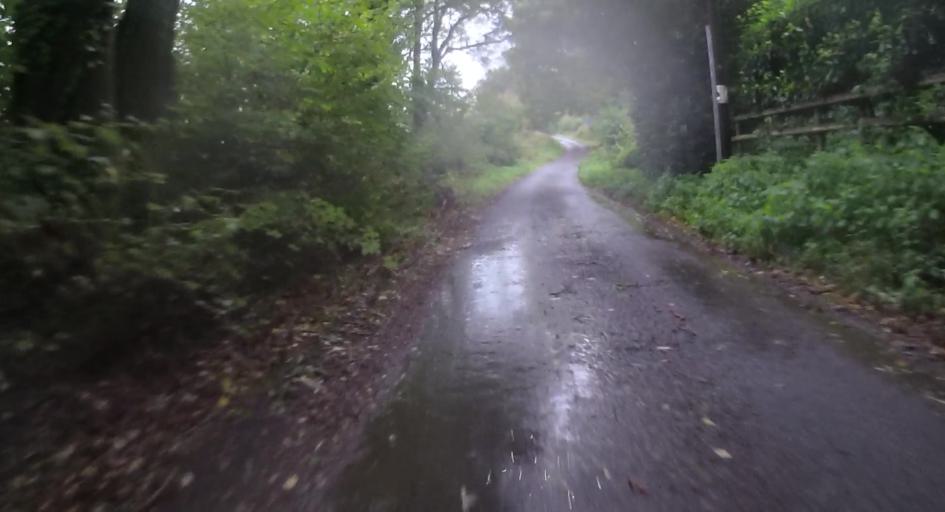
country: GB
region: England
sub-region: Hampshire
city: Tadley
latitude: 51.3522
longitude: -1.1769
